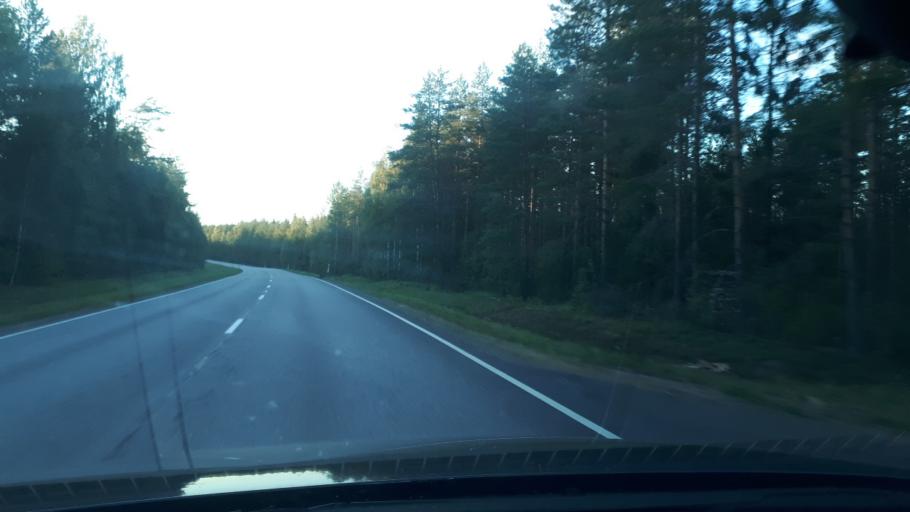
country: FI
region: Northern Ostrobothnia
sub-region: Haapavesi-Siikalatva
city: Pulkkila
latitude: 64.2406
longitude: 25.8942
